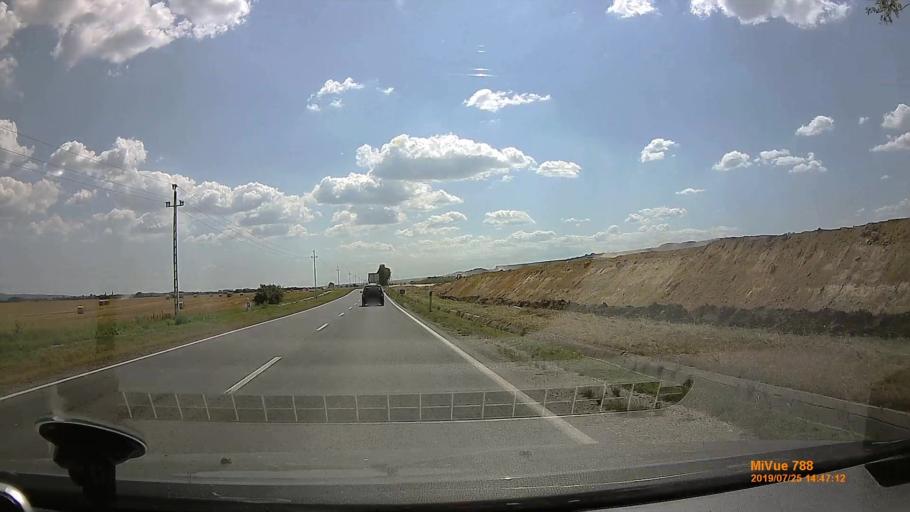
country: HU
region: Borsod-Abauj-Zemplen
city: Halmaj
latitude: 48.2489
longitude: 20.9767
